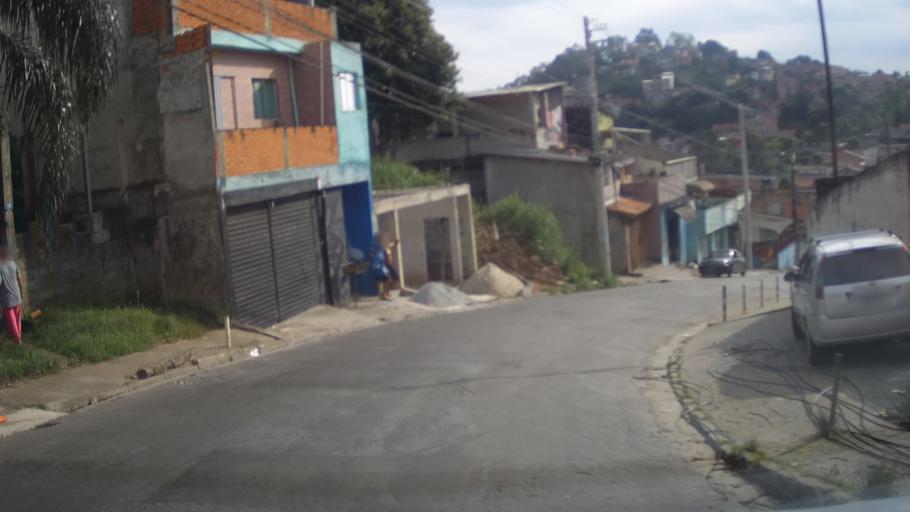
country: BR
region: Sao Paulo
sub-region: Guarulhos
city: Guarulhos
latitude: -23.4036
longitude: -46.5157
